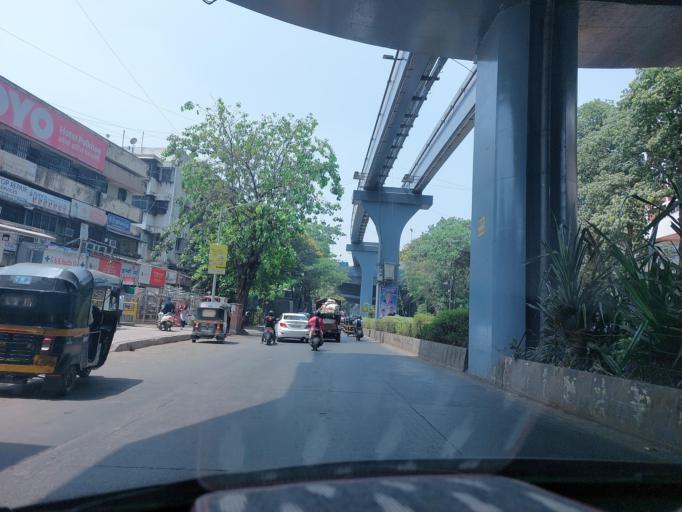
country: IN
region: Maharashtra
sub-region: Mumbai Suburban
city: Mumbai
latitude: 19.0611
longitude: 72.8975
